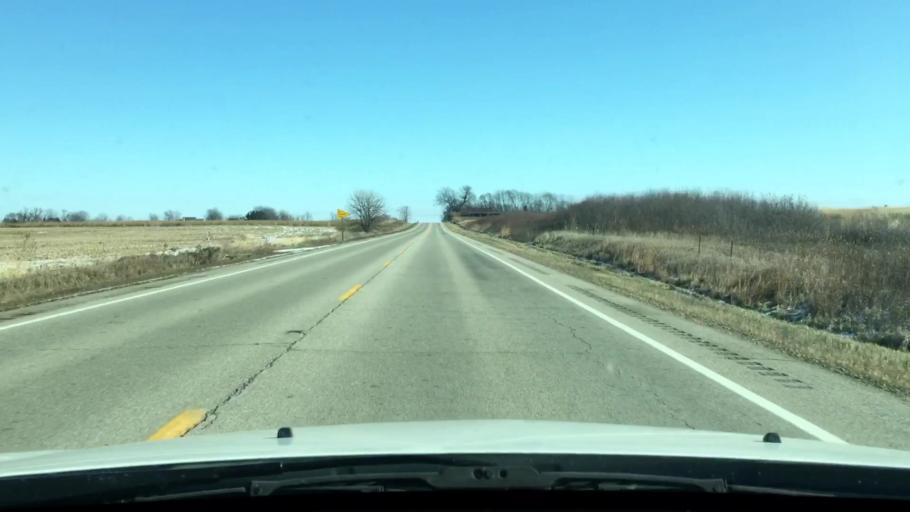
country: US
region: Illinois
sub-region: DeKalb County
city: Malta
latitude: 42.0009
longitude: -88.9063
